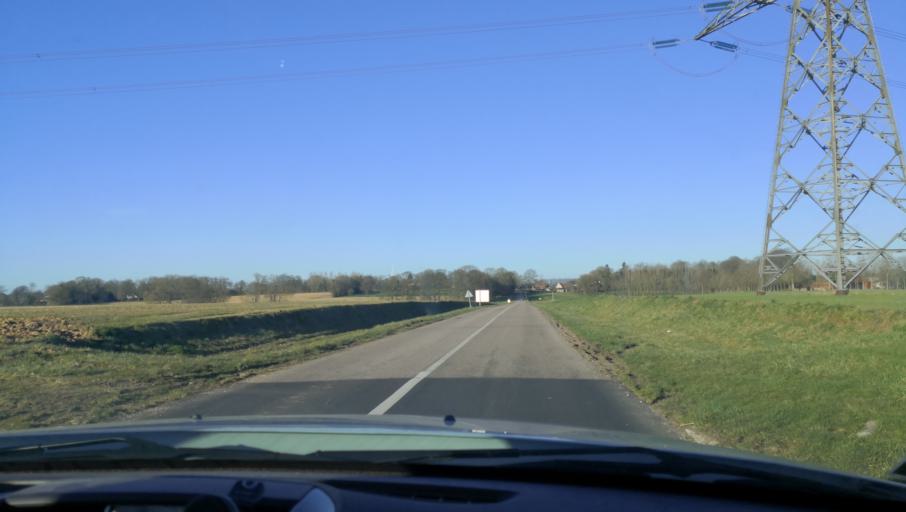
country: FR
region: Haute-Normandie
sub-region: Departement de la Seine-Maritime
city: Totes
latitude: 49.6569
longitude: 1.0211
